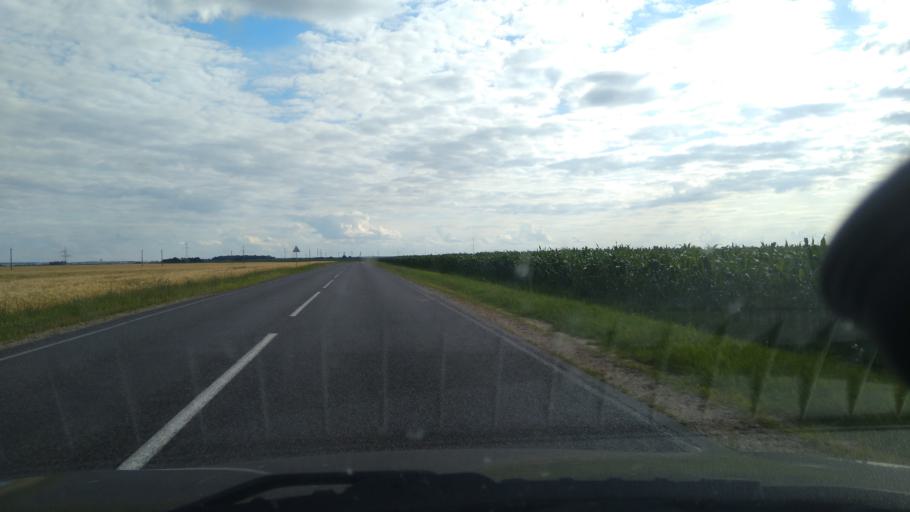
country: BY
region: Grodnenskaya
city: Masty
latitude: 53.3093
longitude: 24.6952
